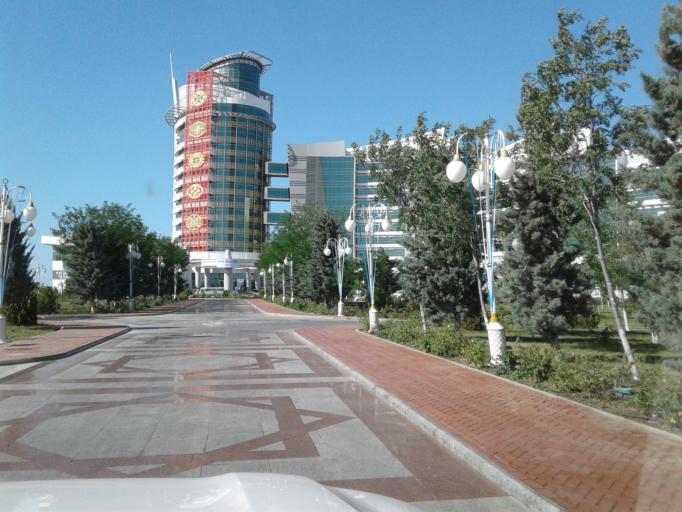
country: TM
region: Balkan
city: Turkmenbasy
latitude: 39.9622
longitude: 52.8350
